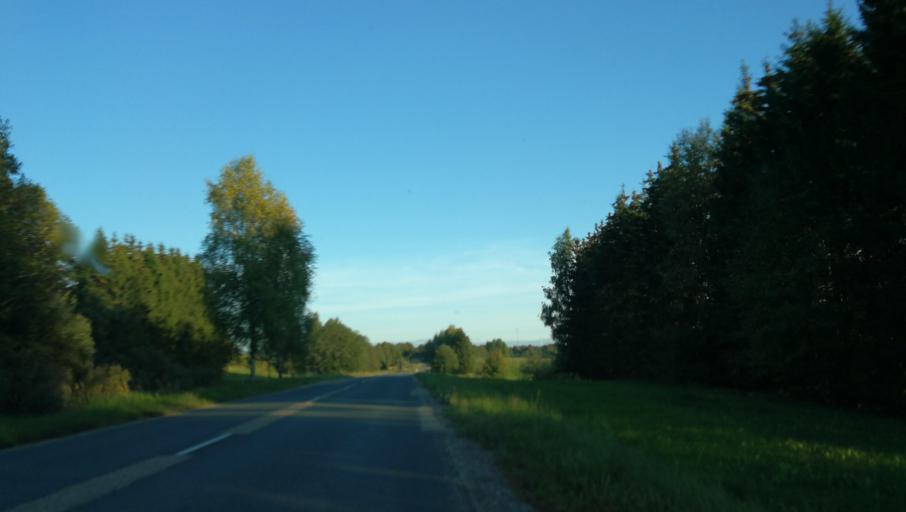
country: LV
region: Aizpute
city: Aizpute
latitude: 56.6211
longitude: 21.7204
